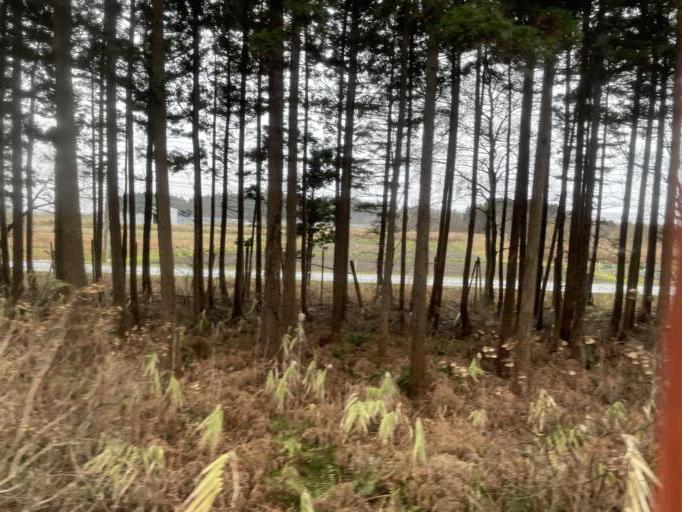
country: JP
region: Aomori
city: Aomori Shi
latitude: 40.9845
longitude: 140.6533
